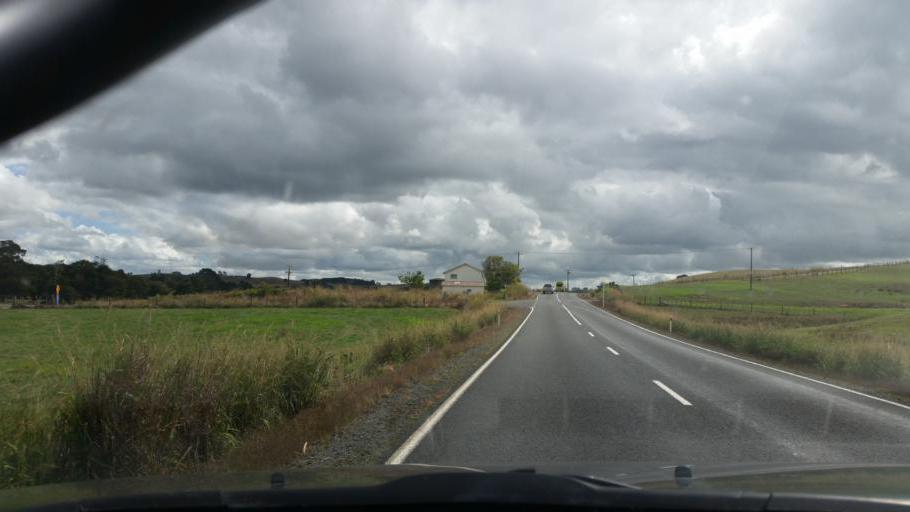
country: NZ
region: Northland
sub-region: Whangarei
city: Ruakaka
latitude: -35.9646
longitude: 174.2911
